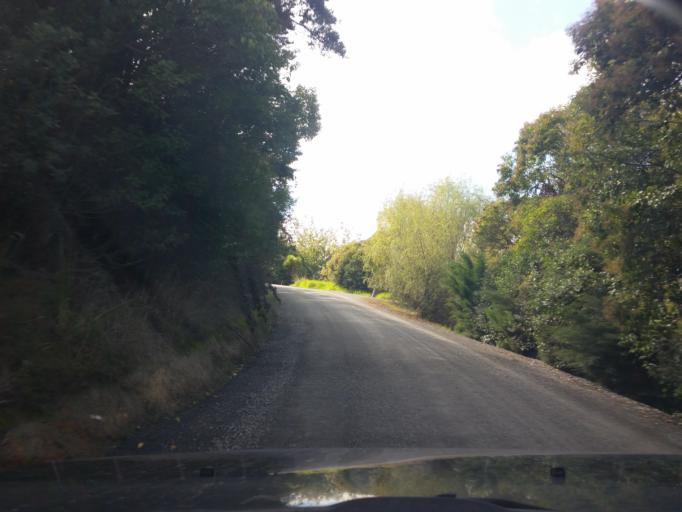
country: NZ
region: Northland
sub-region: Kaipara District
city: Dargaville
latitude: -35.9955
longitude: 173.9522
